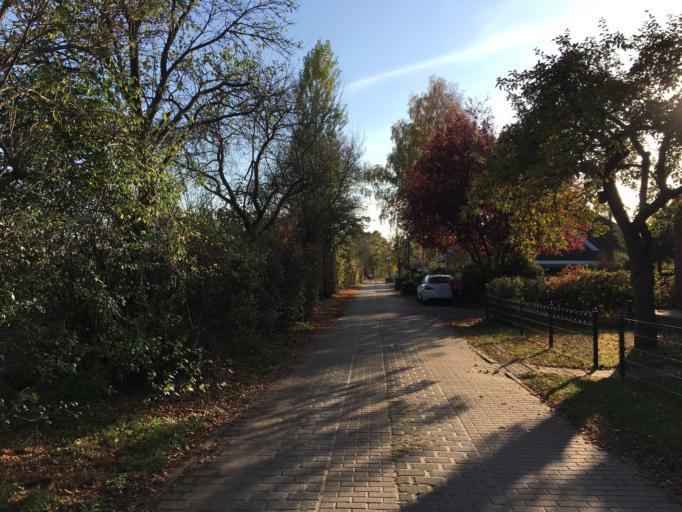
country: DE
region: Lower Saxony
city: Radbruch
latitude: 53.3152
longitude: 10.2918
